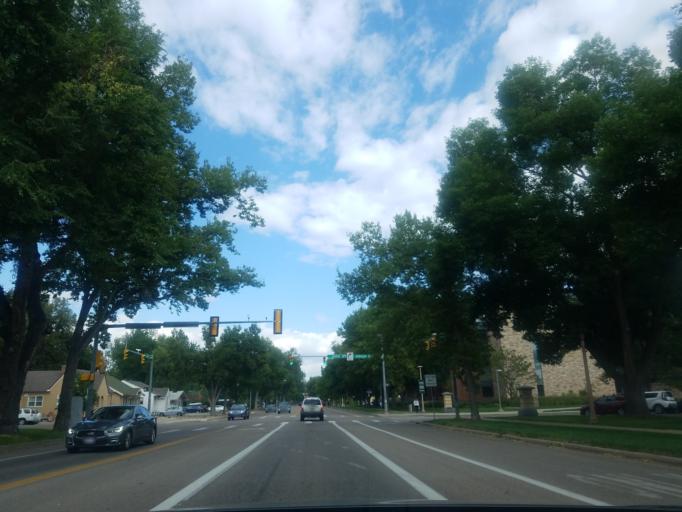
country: US
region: Colorado
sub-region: Larimer County
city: Fort Collins
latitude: 40.5781
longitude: -105.0885
